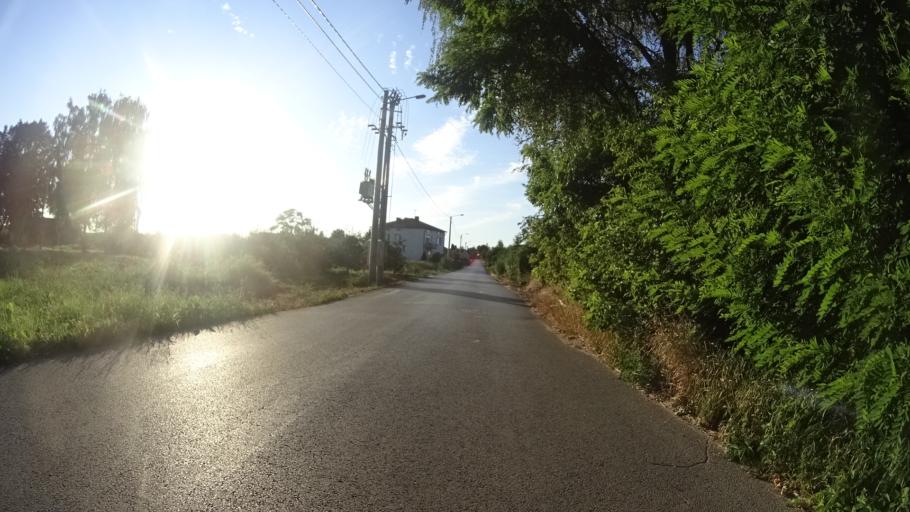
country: PL
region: Masovian Voivodeship
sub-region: Powiat grojecki
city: Goszczyn
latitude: 51.6977
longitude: 20.8100
